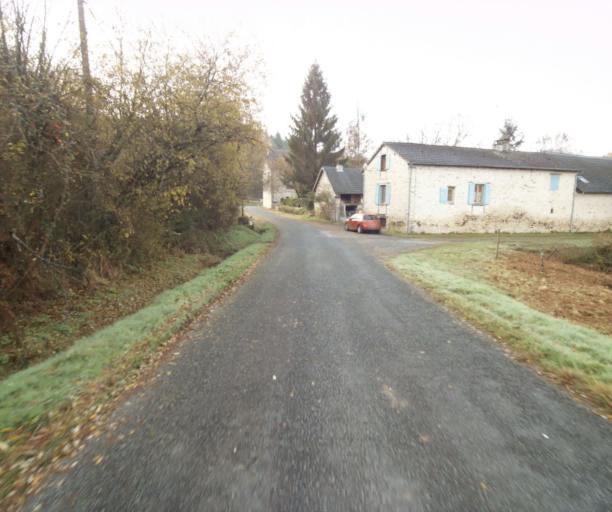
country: FR
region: Limousin
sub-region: Departement de la Correze
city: Chameyrat
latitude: 45.2224
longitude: 1.7223
